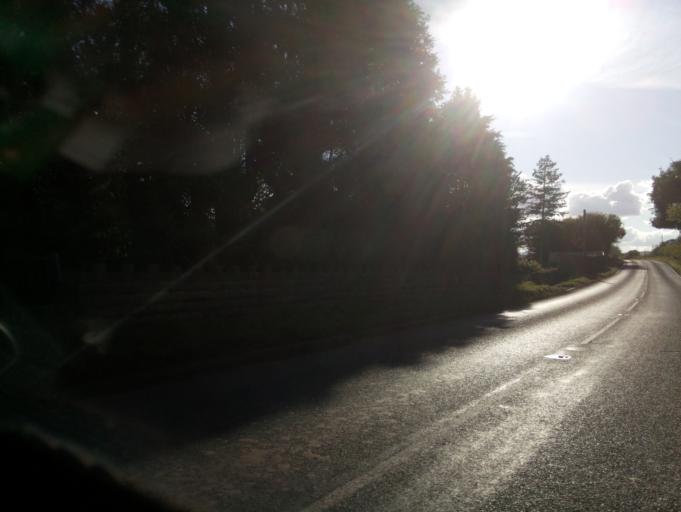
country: GB
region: Wales
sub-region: Sir Powys
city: Hay
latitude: 52.0212
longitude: -3.2222
